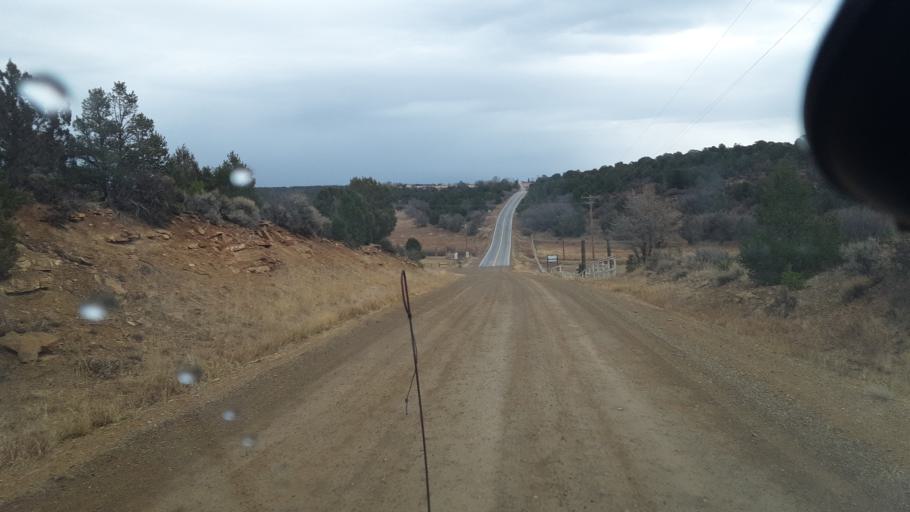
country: US
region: Colorado
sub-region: Montezuma County
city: Mancos
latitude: 37.1984
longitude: -108.1255
